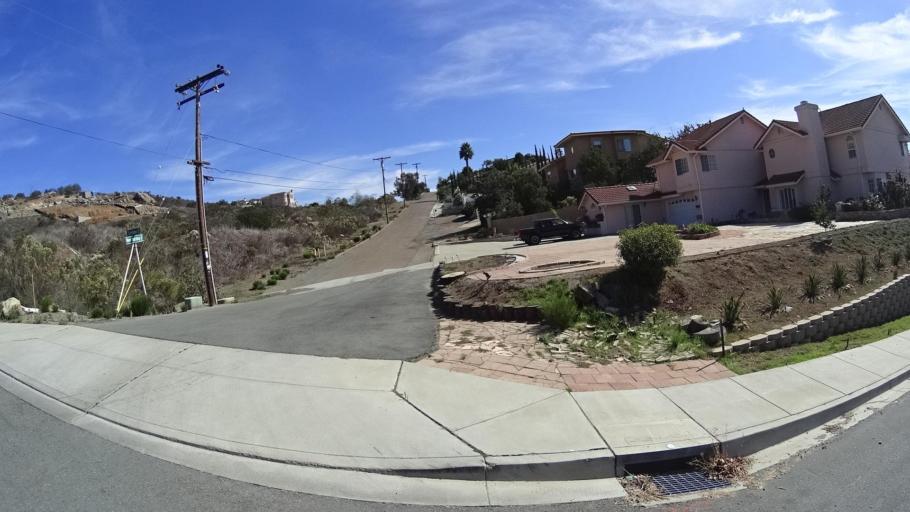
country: US
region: California
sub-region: San Diego County
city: Casa de Oro-Mount Helix
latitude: 32.7534
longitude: -116.9535
